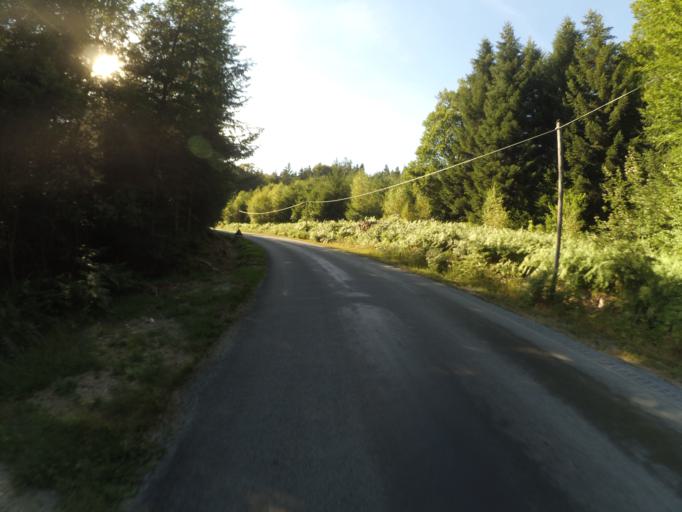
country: FR
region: Limousin
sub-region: Departement de la Creuse
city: Banize
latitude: 45.7844
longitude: 1.9826
